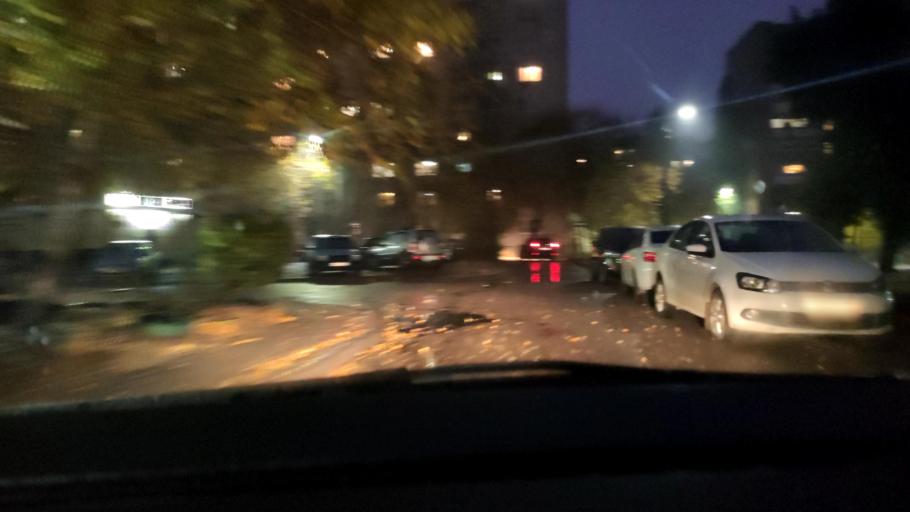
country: RU
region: Voronezj
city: Podgornoye
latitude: 51.6983
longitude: 39.1414
